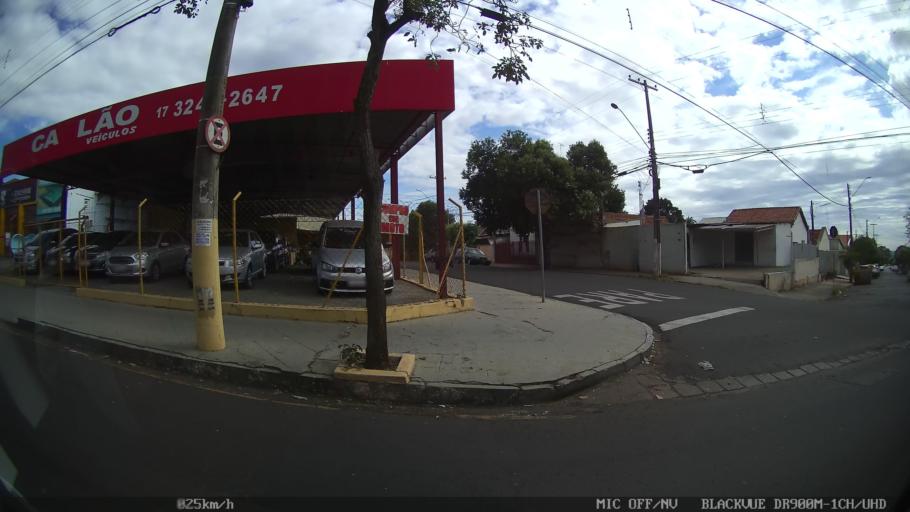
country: BR
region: Sao Paulo
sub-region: Bady Bassitt
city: Bady Bassitt
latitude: -20.8106
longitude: -49.5087
